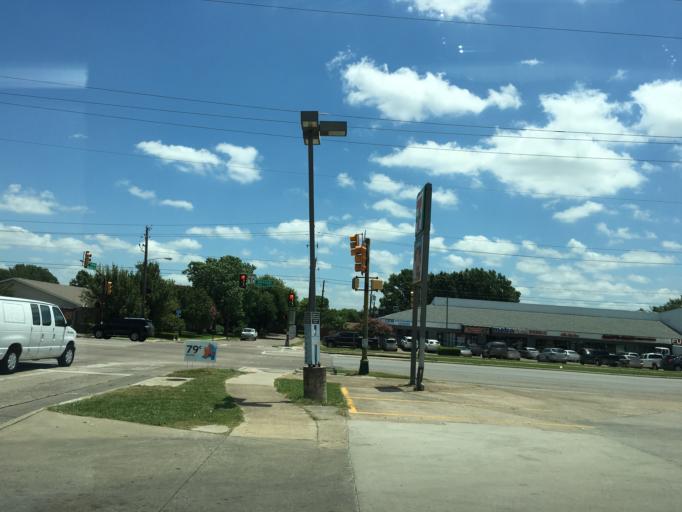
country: US
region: Texas
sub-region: Dallas County
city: Garland
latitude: 32.8505
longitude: -96.6663
